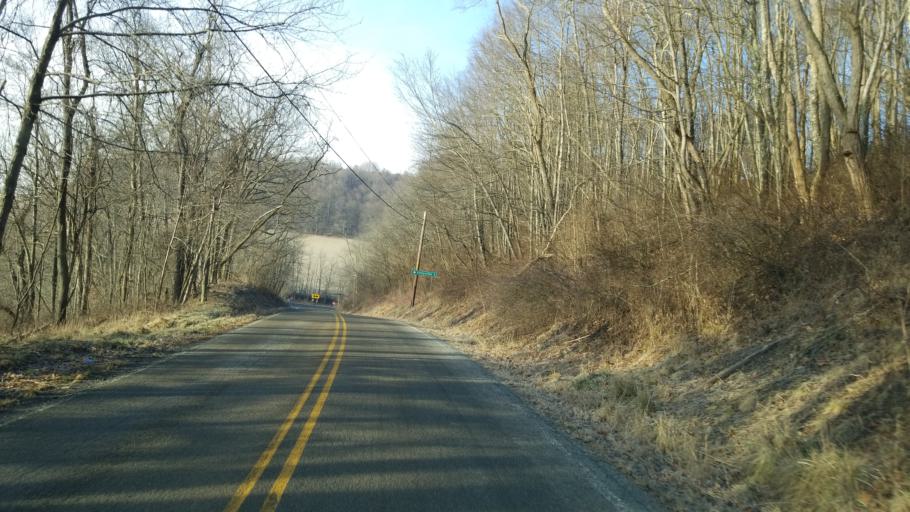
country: US
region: Pennsylvania
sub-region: Jefferson County
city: Brookville
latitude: 40.9639
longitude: -79.2558
